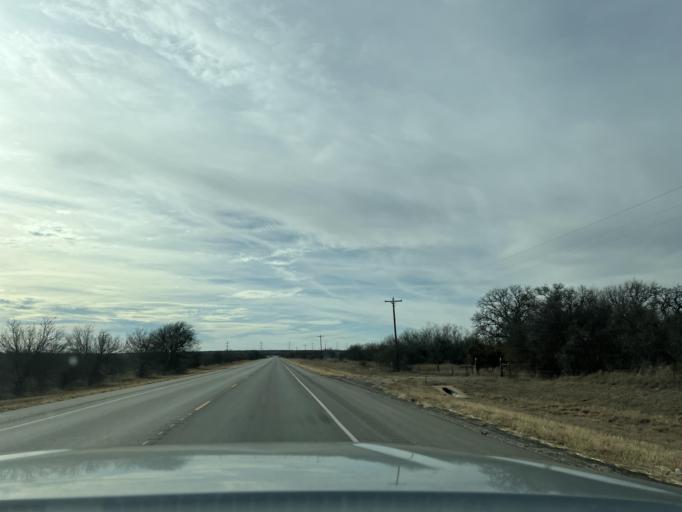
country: US
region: Texas
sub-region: Jones County
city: Stamford
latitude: 32.7559
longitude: -99.6120
